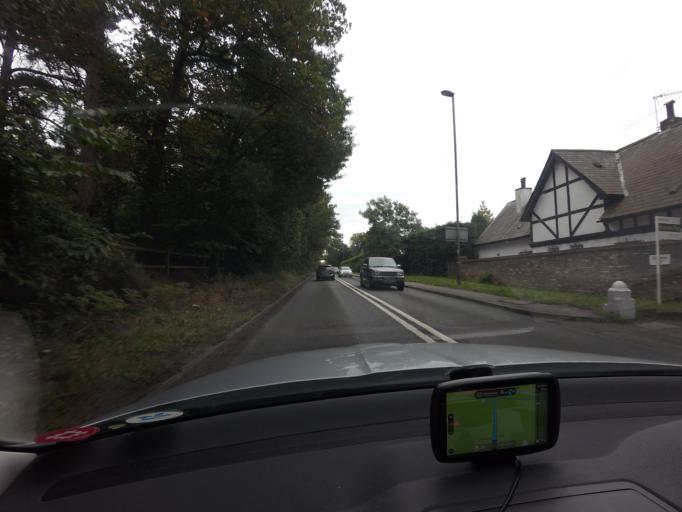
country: GB
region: England
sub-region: Surrey
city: Byfleet
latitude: 51.3378
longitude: -0.4460
